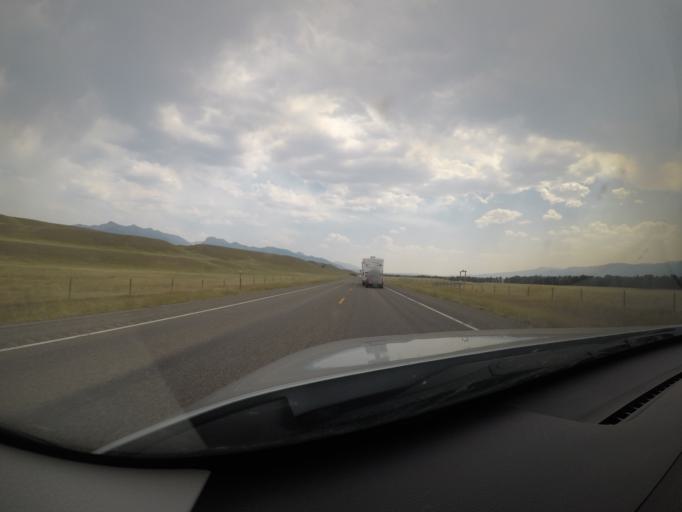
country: US
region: Montana
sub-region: Gallatin County
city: Big Sky
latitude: 45.1107
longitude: -111.6555
